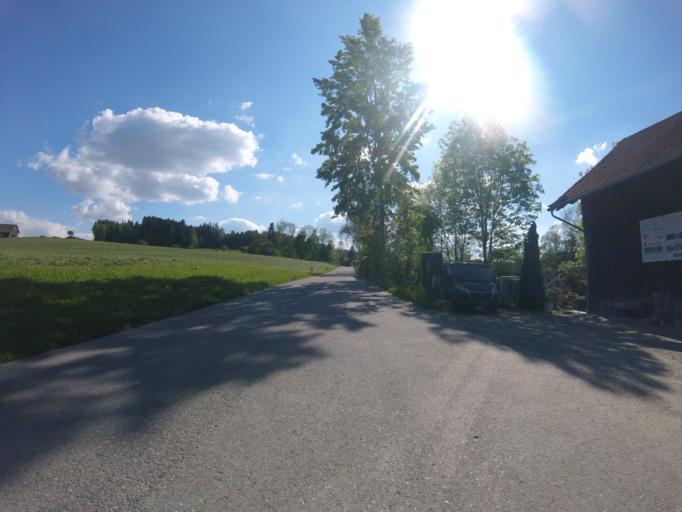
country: CH
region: Saint Gallen
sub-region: Wahlkreis Wil
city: Degersheim
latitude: 47.3972
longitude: 9.2168
